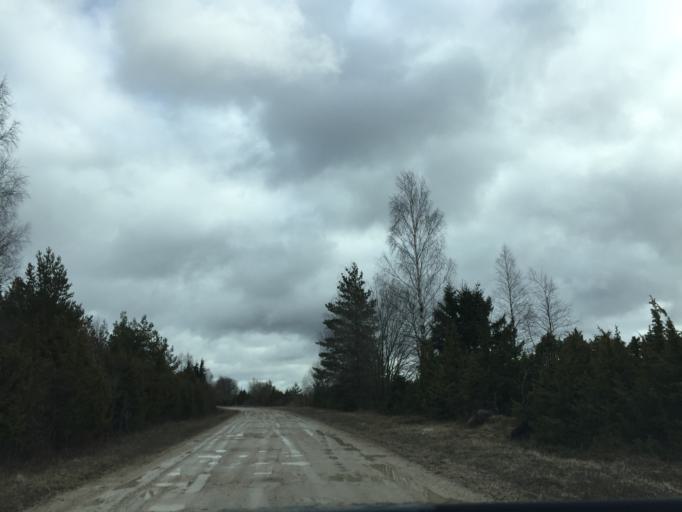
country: EE
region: Laeaene
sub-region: Ridala Parish
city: Uuemoisa
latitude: 58.6862
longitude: 23.5463
